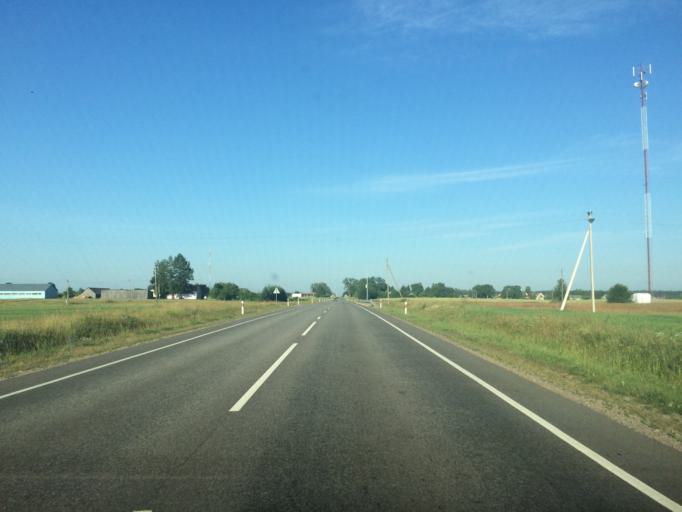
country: LT
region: Vilnius County
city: Ukmerge
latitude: 55.1691
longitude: 24.5264
